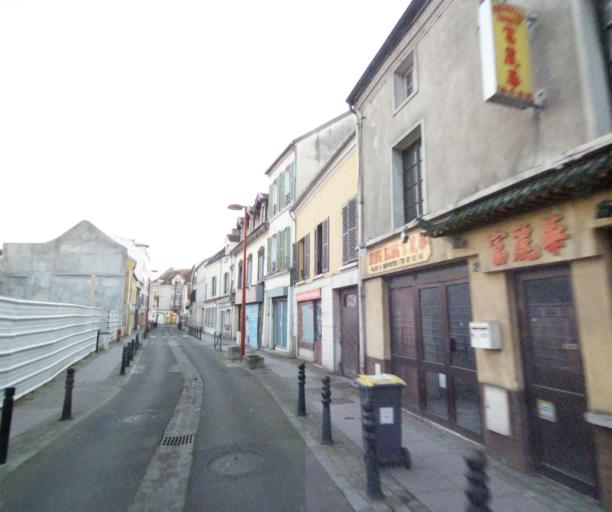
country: FR
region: Ile-de-France
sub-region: Departement du Val-d'Oise
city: Gonesse
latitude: 48.9867
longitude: 2.4469
